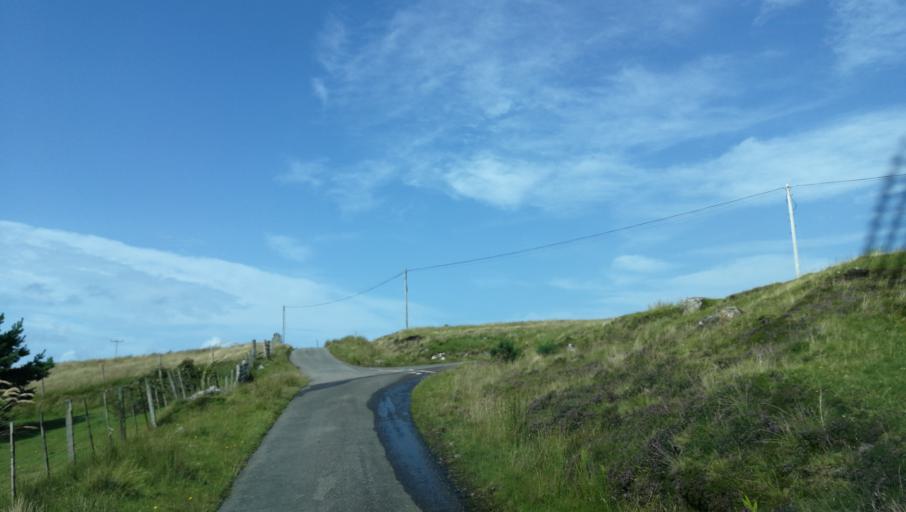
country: GB
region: Scotland
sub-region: Highland
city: Portree
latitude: 57.7466
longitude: -5.7754
